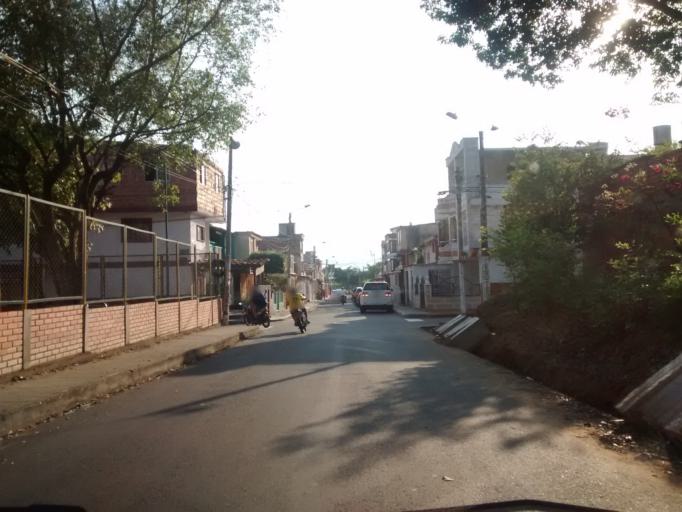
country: CO
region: Santander
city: Bucaramanga
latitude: 7.0994
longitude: -73.1315
